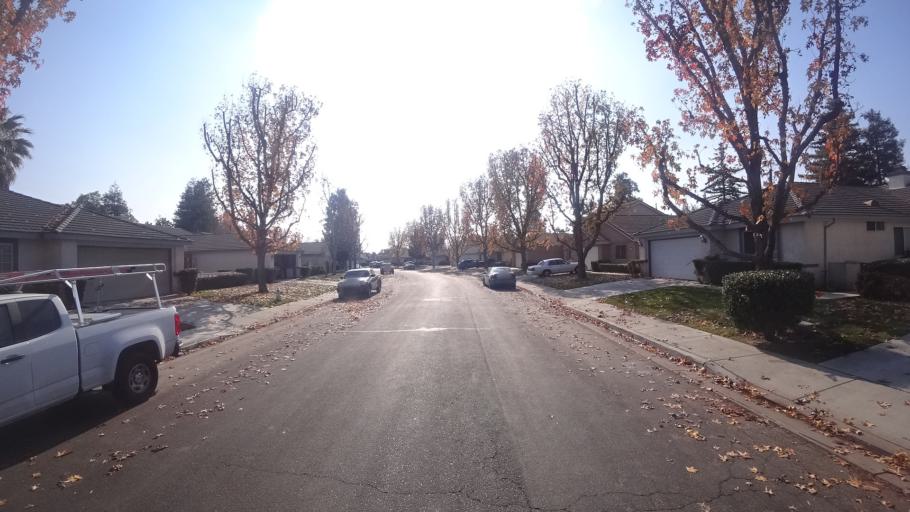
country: US
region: California
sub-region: Kern County
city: Greenacres
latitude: 35.3093
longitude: -119.0871
